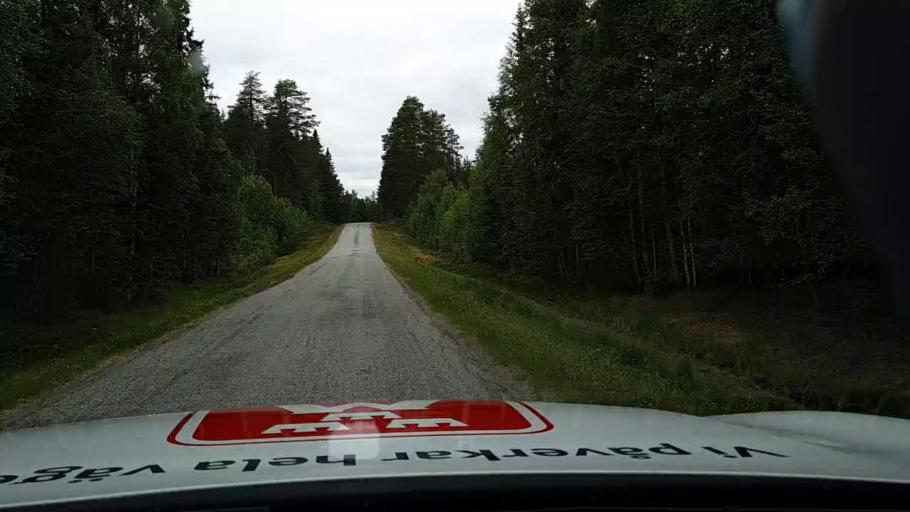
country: SE
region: Vaesterbotten
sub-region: Dorotea Kommun
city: Dorotea
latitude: 64.0961
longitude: 16.4193
